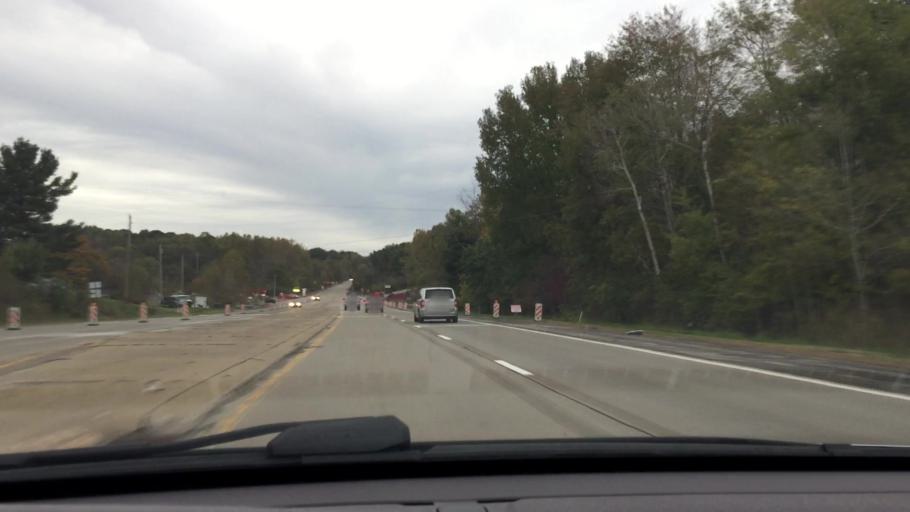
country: US
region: Pennsylvania
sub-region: Lawrence County
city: Oakwood
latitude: 41.0365
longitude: -80.4077
